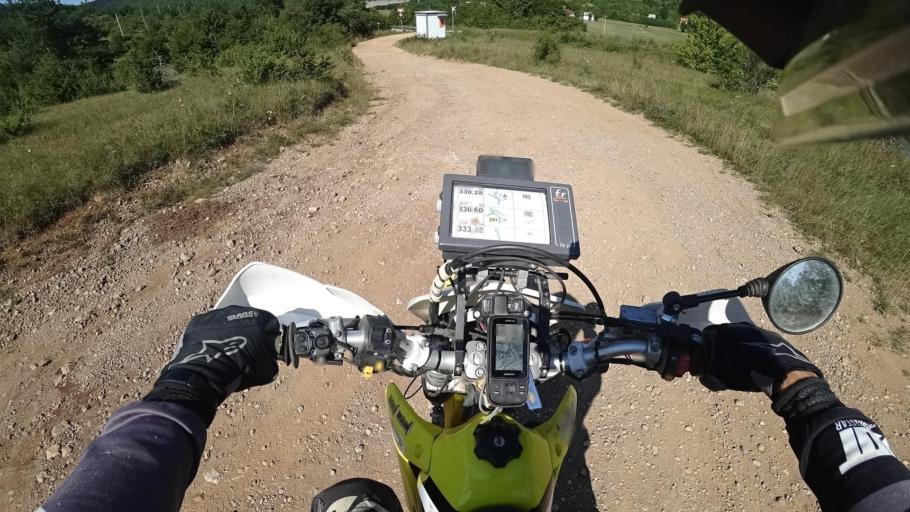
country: HR
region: Licko-Senjska
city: Jezerce
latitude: 44.8628
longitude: 15.4440
